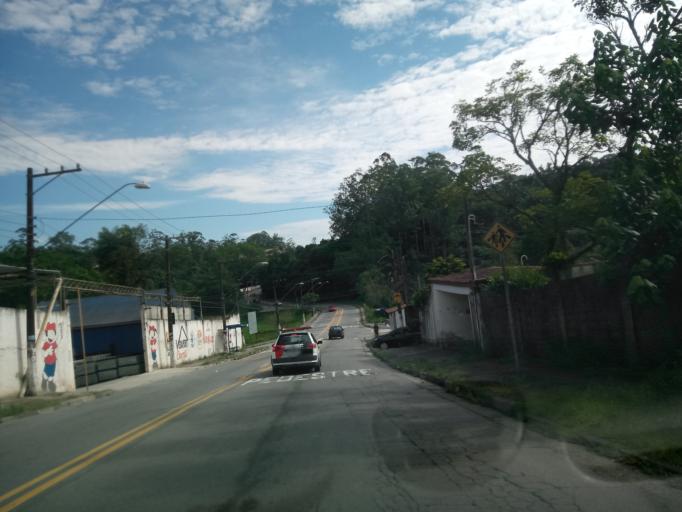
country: BR
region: Sao Paulo
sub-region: Sao Bernardo Do Campo
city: Sao Bernardo do Campo
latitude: -23.7914
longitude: -46.5388
